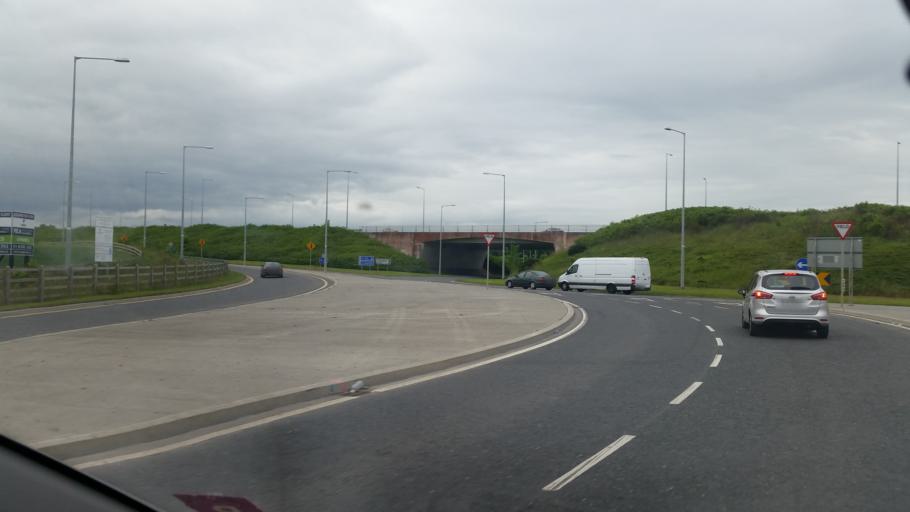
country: IE
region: Leinster
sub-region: Fingal County
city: Blanchardstown
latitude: 53.4319
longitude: -6.3472
